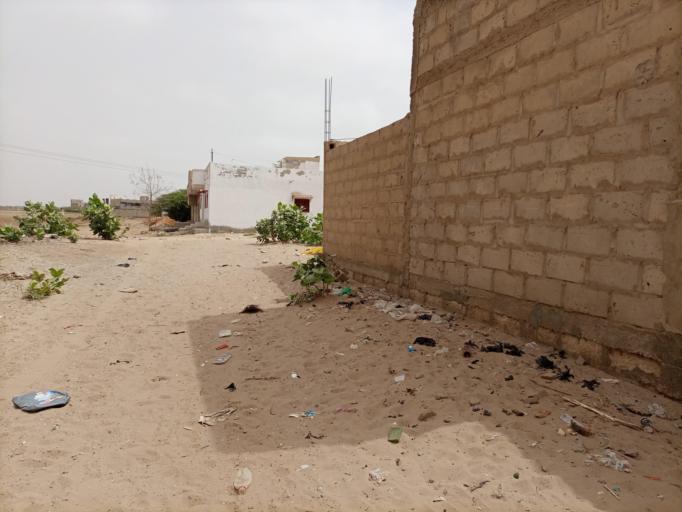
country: SN
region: Saint-Louis
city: Saint-Louis
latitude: 16.0378
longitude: -16.4401
